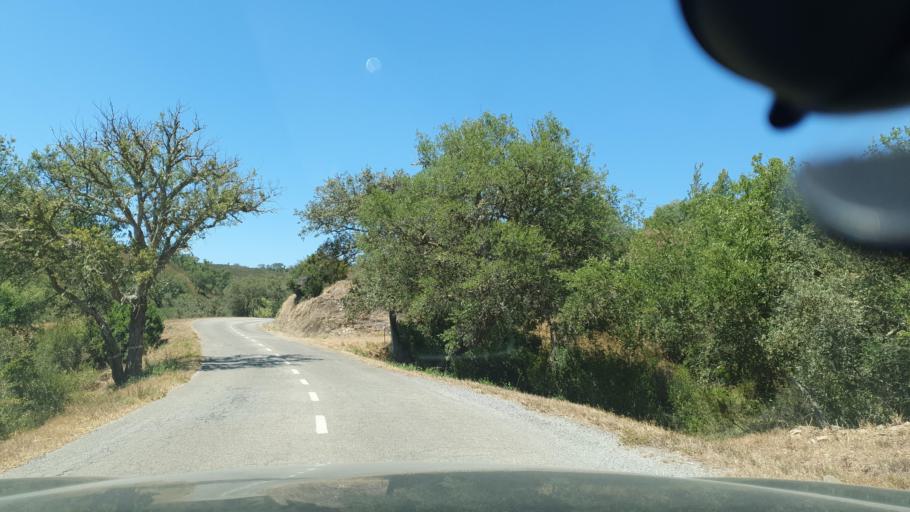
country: PT
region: Beja
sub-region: Odemira
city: Odemira
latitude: 37.6052
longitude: -8.5929
